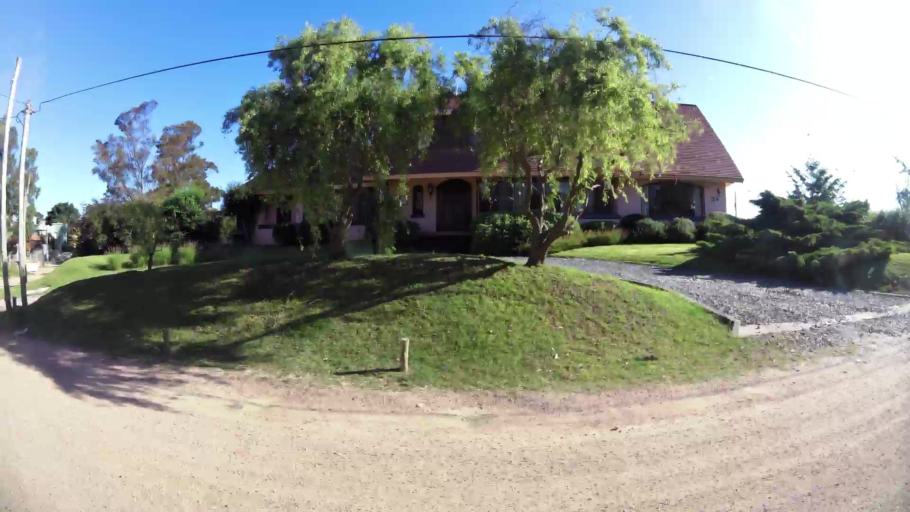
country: UY
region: Canelones
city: Barra de Carrasco
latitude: -34.8622
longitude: -56.0299
